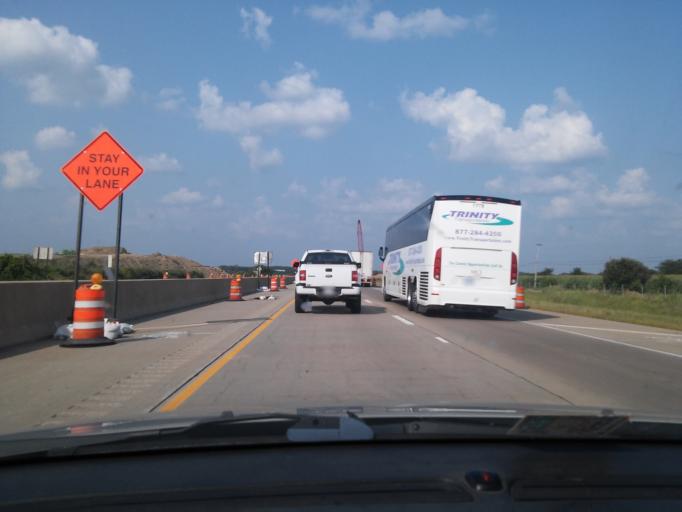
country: US
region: Illinois
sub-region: Grundy County
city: Minooka
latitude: 41.4523
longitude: -88.3199
